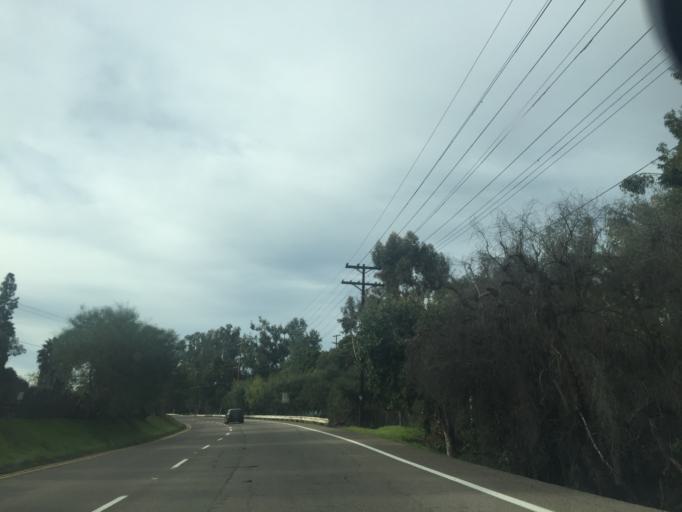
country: US
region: California
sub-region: San Diego County
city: Lemon Grove
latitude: 32.7598
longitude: -117.1005
